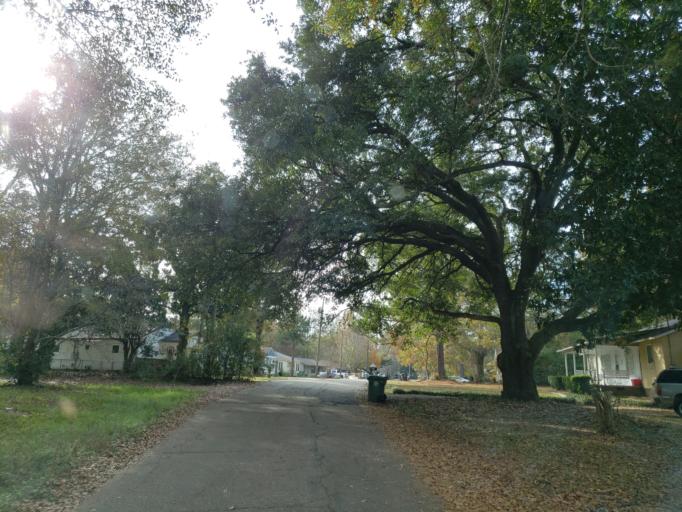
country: US
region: Mississippi
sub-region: Forrest County
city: Hattiesburg
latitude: 31.3343
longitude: -89.3143
